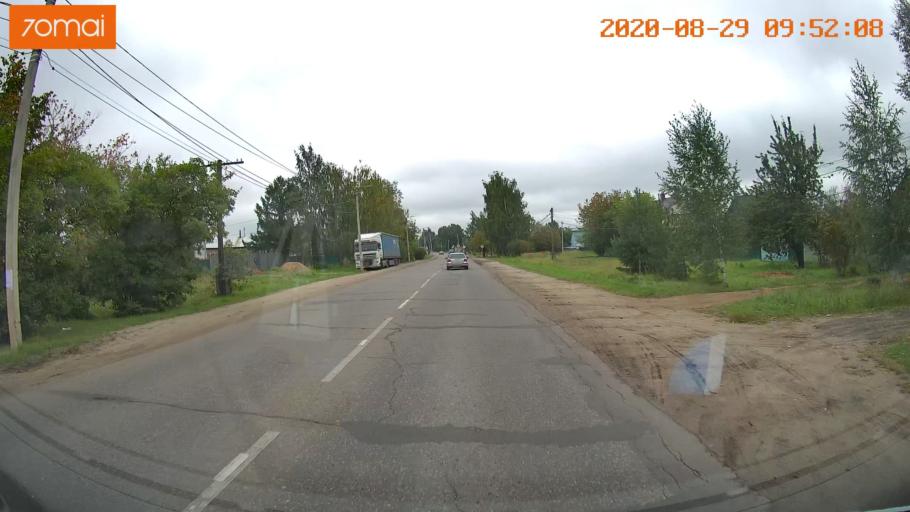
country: RU
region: Ivanovo
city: Kineshma
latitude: 57.4251
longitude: 42.2058
